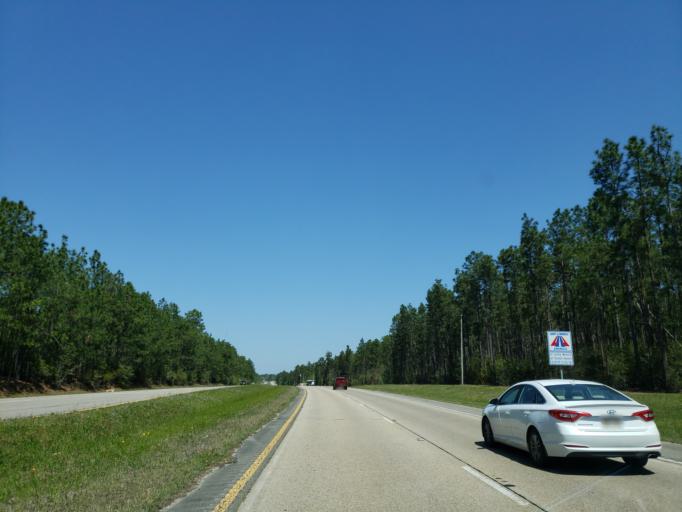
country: US
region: Mississippi
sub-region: Harrison County
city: Saucier
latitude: 30.6036
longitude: -89.1277
